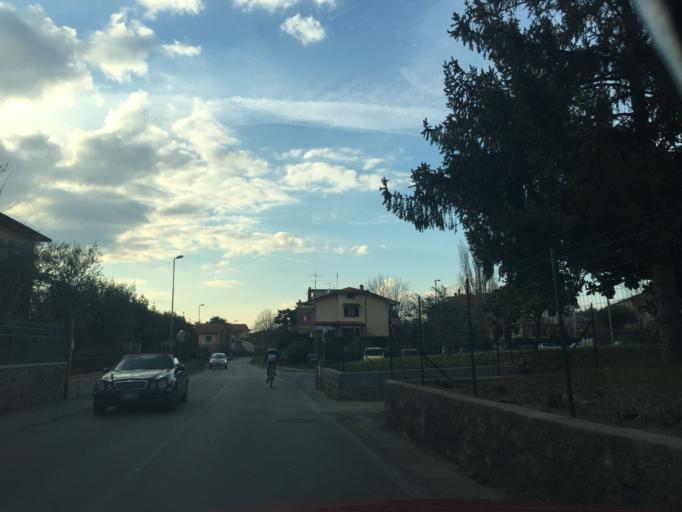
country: IT
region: Tuscany
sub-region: Provincia di Pistoia
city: Cintolese
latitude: 43.8601
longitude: 10.8253
